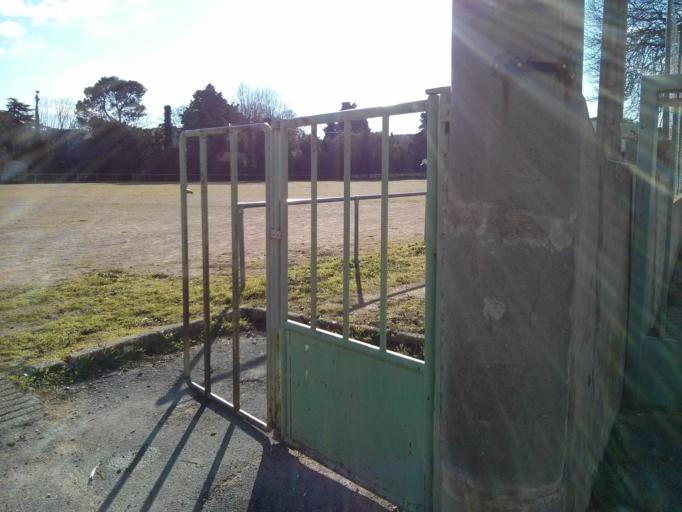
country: FR
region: Languedoc-Roussillon
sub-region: Departement du Gard
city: Aigues-Vives
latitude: 43.7399
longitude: 4.1772
